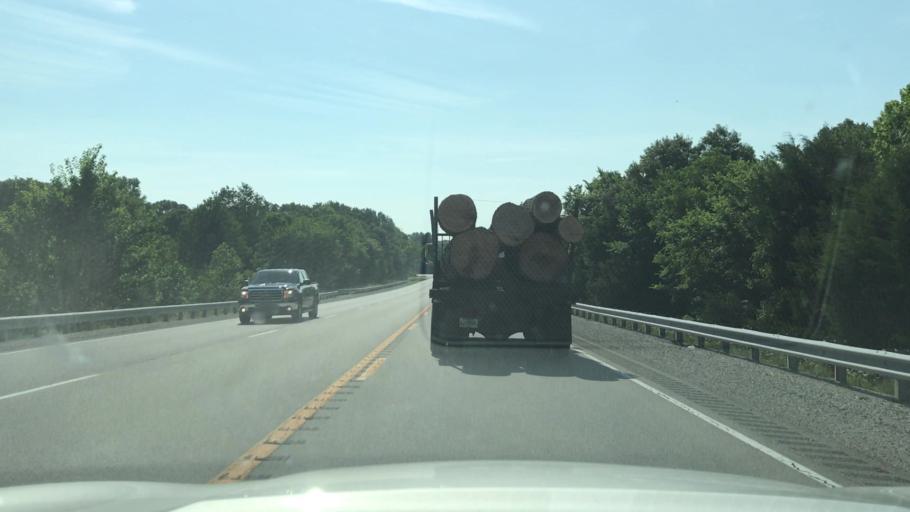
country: US
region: Kentucky
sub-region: Wayne County
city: Monticello
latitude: 36.7653
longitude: -84.9910
